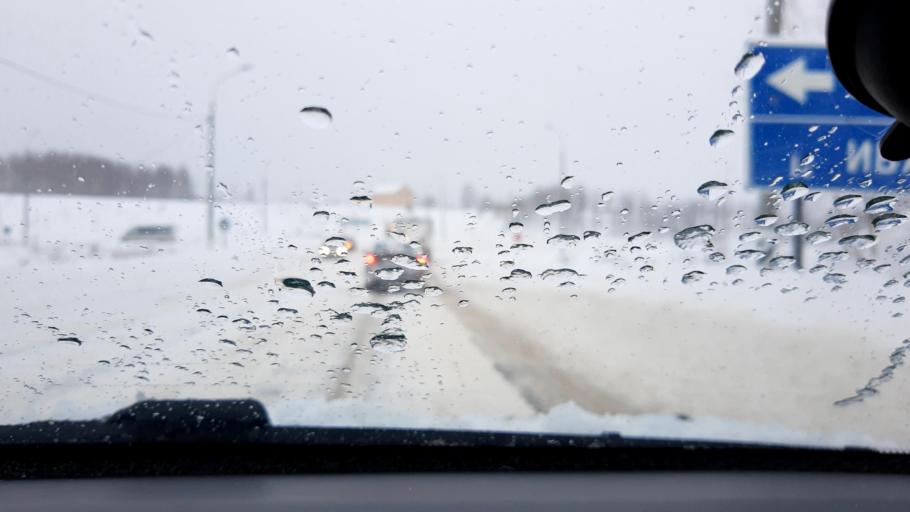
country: RU
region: Nizjnij Novgorod
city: Pervomayskiy
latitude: 56.6323
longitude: 43.2531
